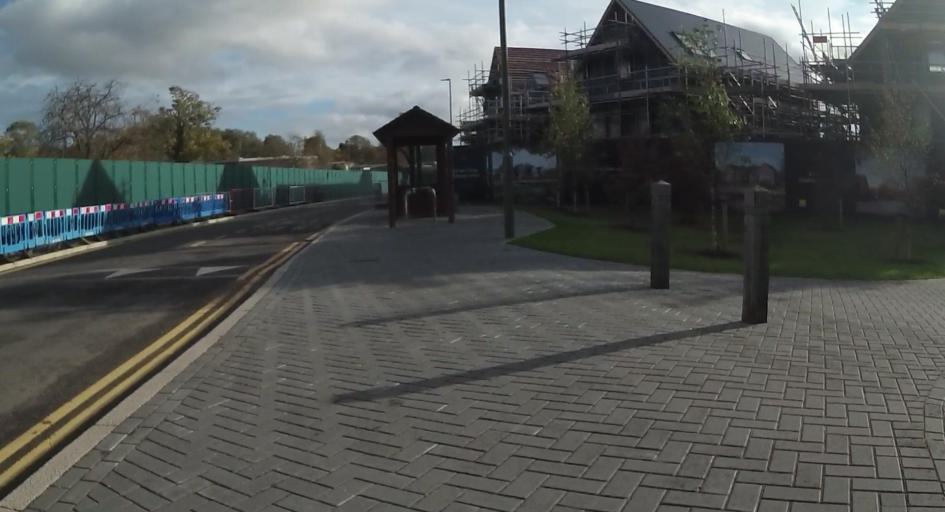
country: GB
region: England
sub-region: Surrey
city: Frimley
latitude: 51.3063
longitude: -0.7040
